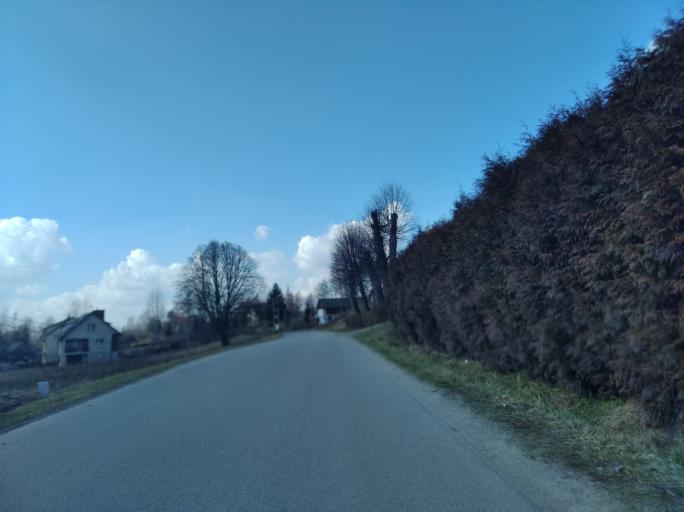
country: PL
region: Subcarpathian Voivodeship
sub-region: Powiat debicki
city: Brzostek
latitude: 49.8845
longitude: 21.4469
